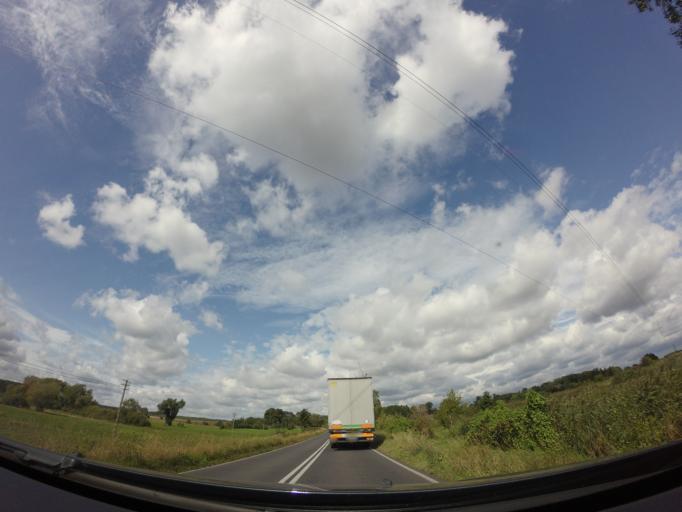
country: PL
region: Lubusz
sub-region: Powiat strzelecko-drezdenecki
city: Dobiegniew
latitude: 52.9810
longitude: 15.7523
